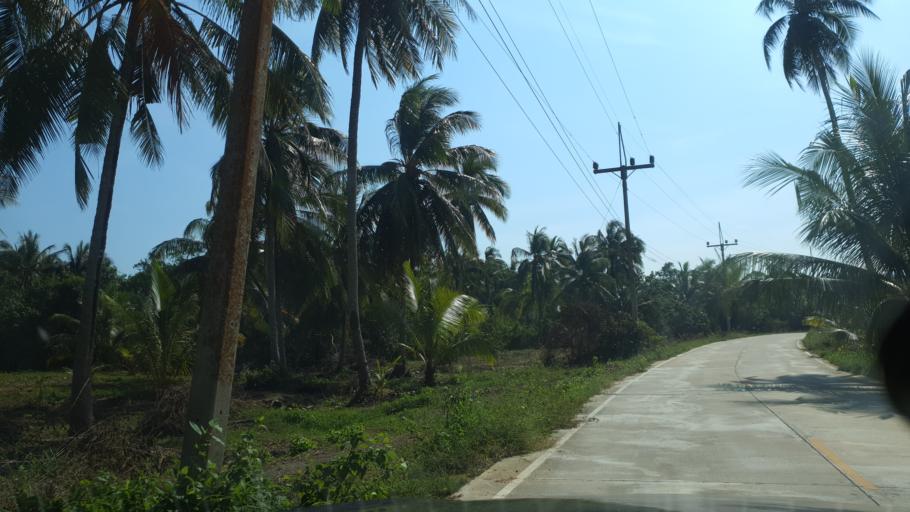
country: TH
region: Surat Thani
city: Tha Chana
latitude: 9.5952
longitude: 99.2051
